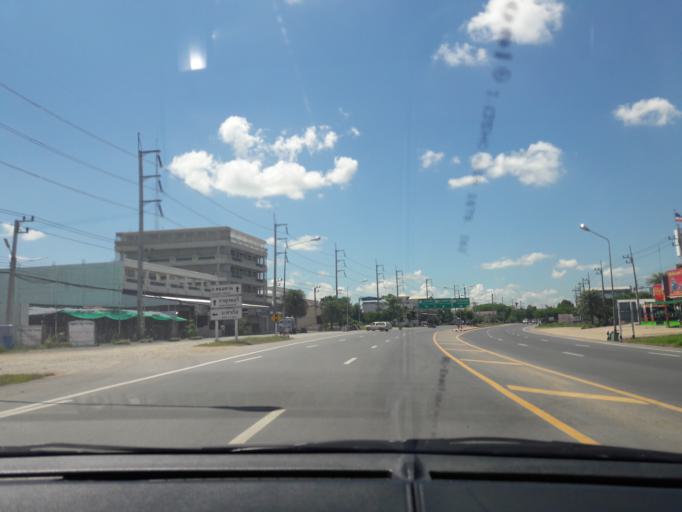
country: TH
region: Kanchanaburi
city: Tha Maka
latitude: 14.0370
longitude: 99.7933
